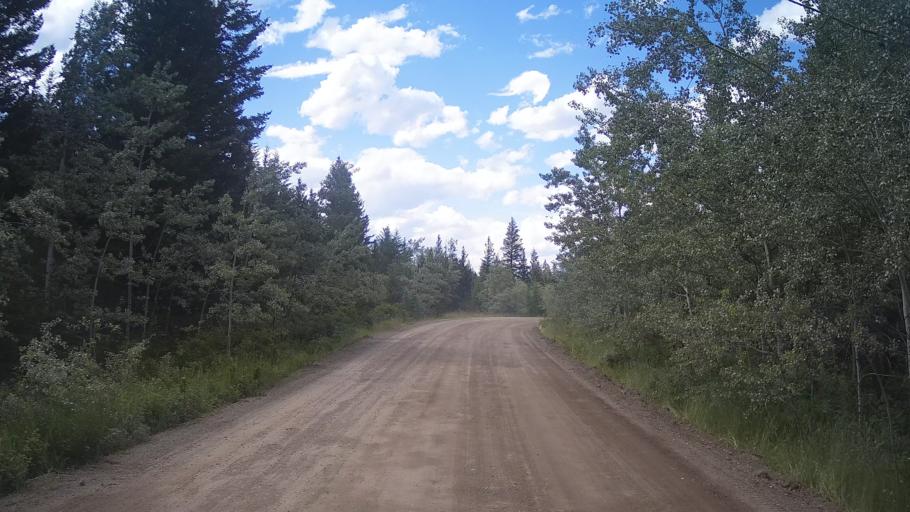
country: CA
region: British Columbia
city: Lillooet
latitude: 51.3358
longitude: -121.9056
